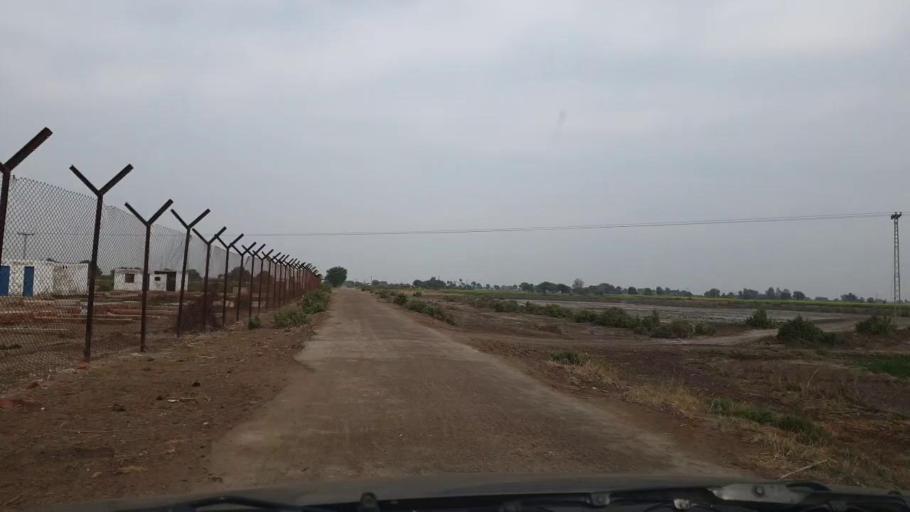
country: PK
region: Sindh
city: Sanghar
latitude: 26.1028
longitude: 68.8963
